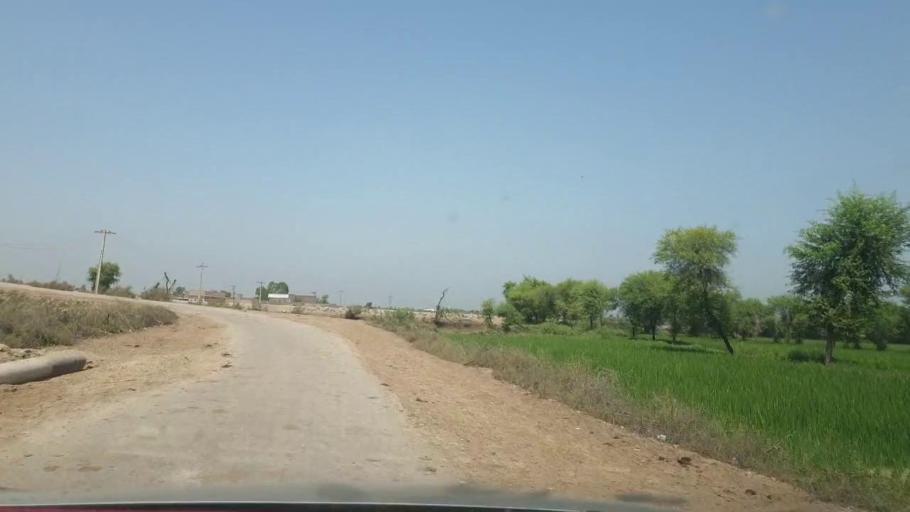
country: PK
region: Sindh
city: Warah
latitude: 27.4822
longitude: 67.7541
